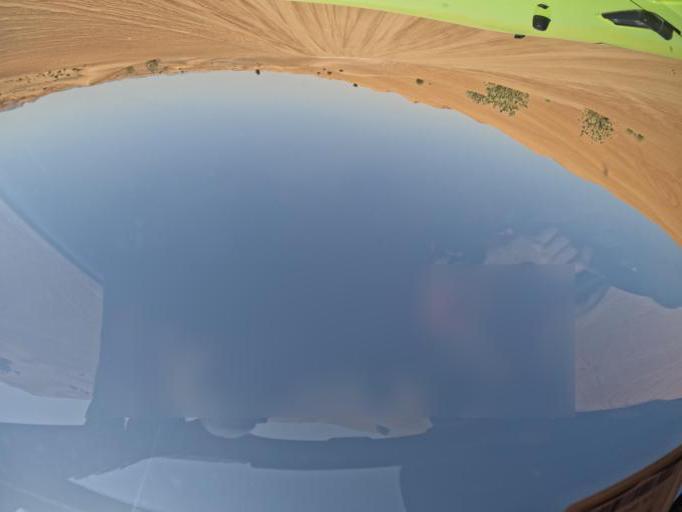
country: AE
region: Ash Shariqah
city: Adh Dhayd
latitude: 24.9974
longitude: 55.7262
